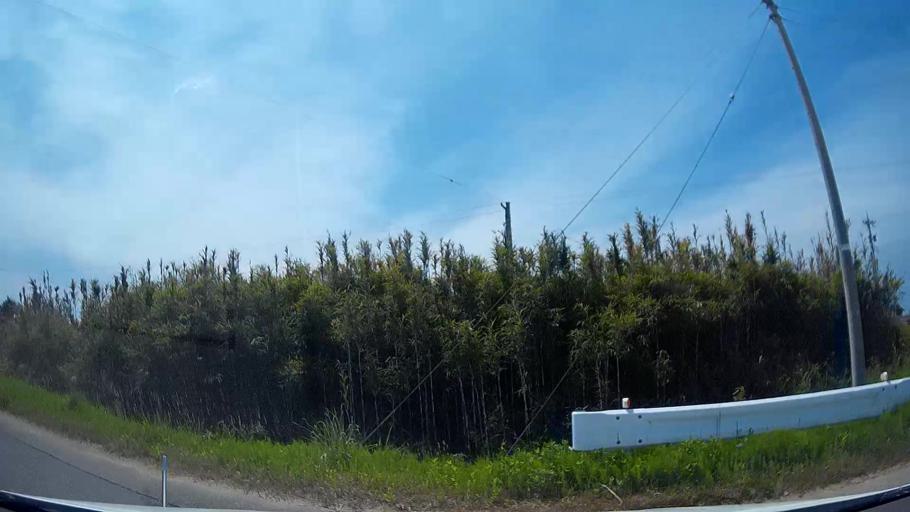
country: JP
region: Ishikawa
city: Hakui
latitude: 36.9459
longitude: 136.7634
